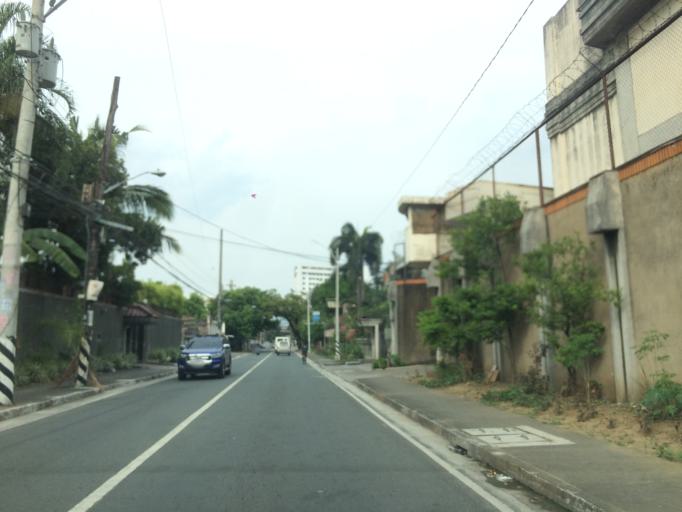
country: PH
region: Calabarzon
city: Del Monte
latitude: 14.6289
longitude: 121.0072
